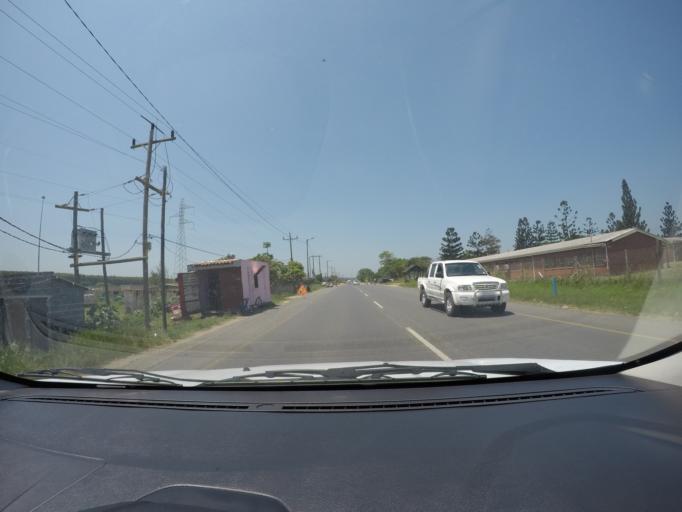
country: ZA
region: KwaZulu-Natal
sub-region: uThungulu District Municipality
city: eSikhawini
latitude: -28.8766
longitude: 31.8944
